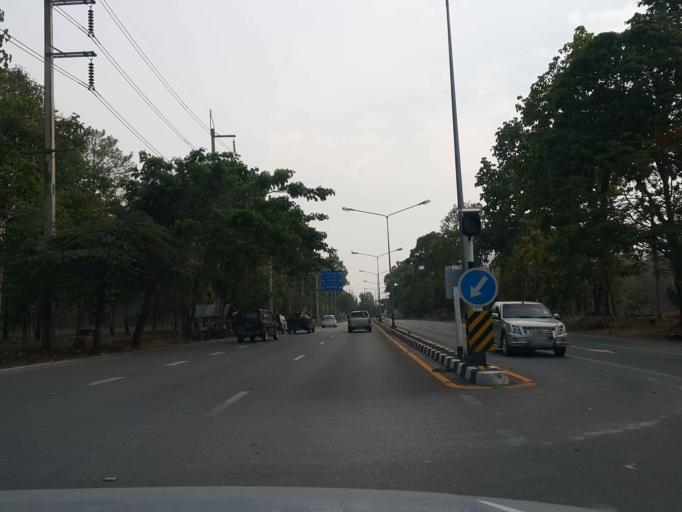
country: TH
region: Chiang Mai
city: Mae Taeng
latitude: 19.1512
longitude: 98.9478
